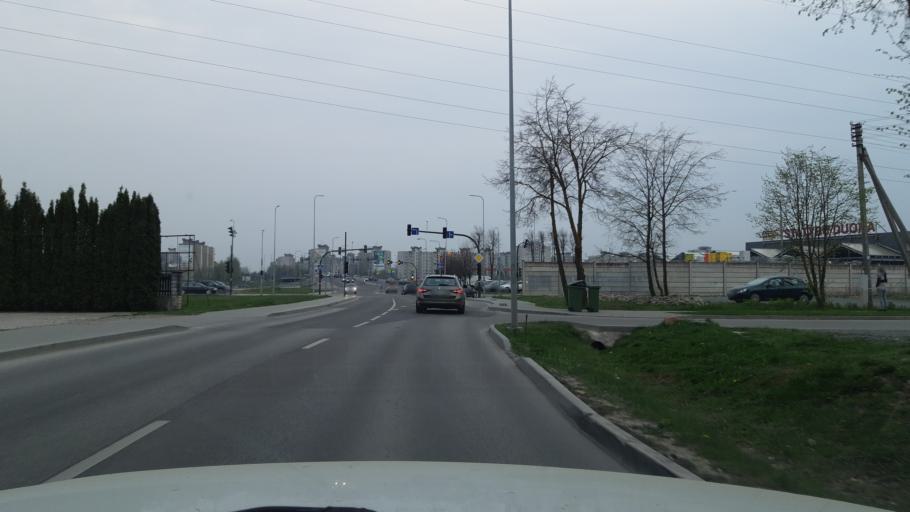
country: LT
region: Kauno apskritis
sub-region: Kaunas
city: Silainiai
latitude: 54.9401
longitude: 23.9003
